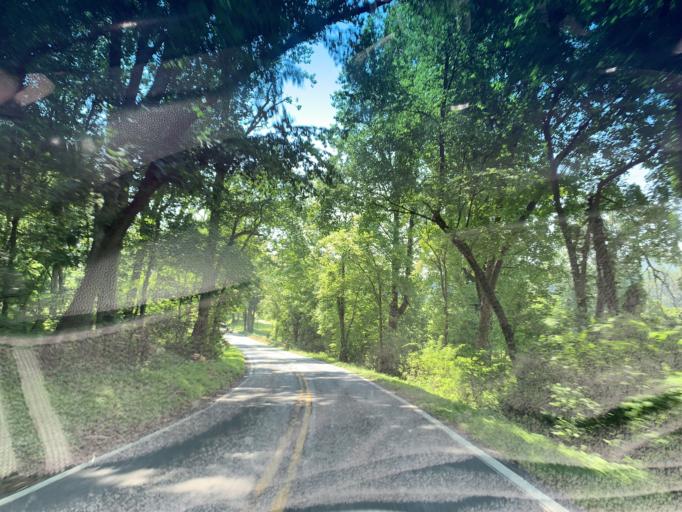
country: US
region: Maryland
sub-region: Frederick County
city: Urbana
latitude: 39.2510
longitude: -77.3747
